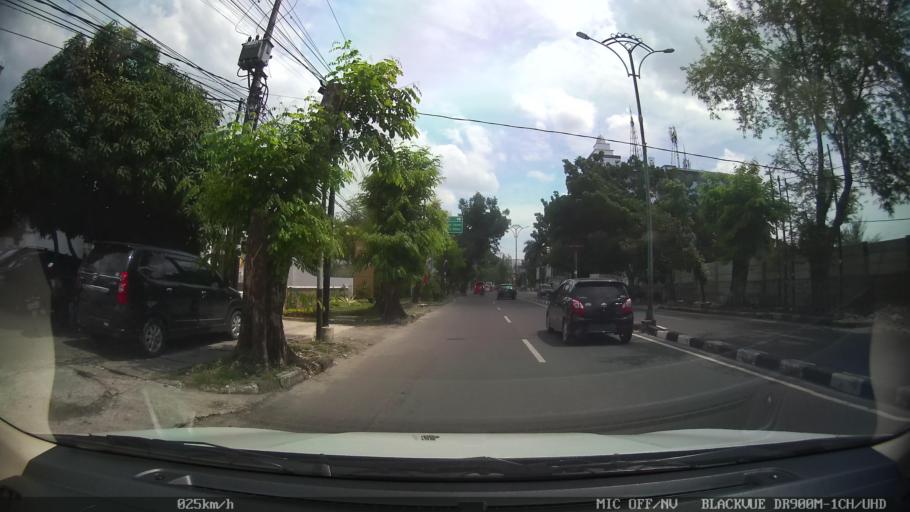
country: ID
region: North Sumatra
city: Medan
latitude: 3.5736
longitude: 98.6603
